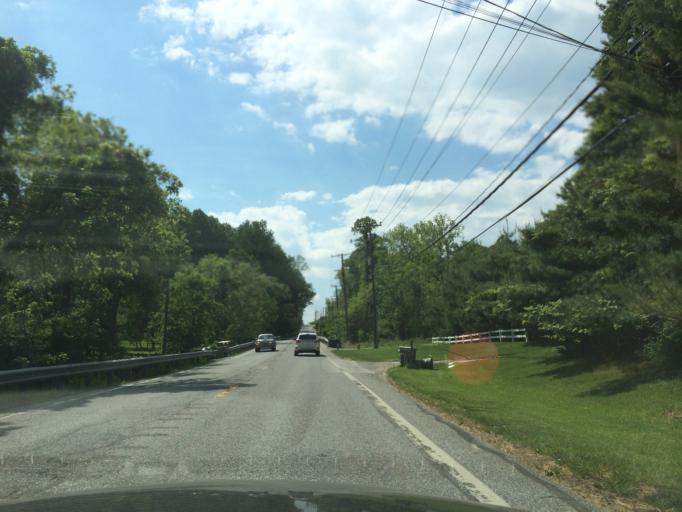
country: US
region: Maryland
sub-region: Carroll County
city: Sykesville
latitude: 39.2976
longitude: -76.9323
